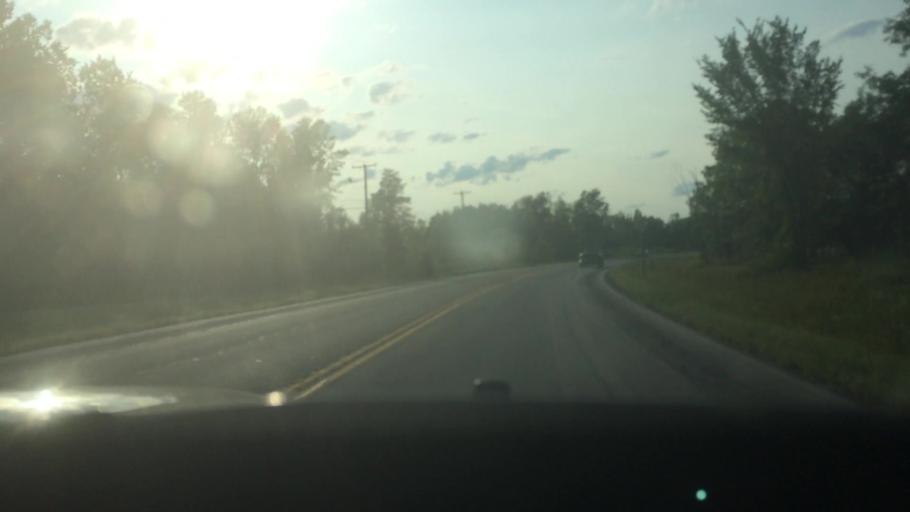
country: US
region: New York
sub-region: St. Lawrence County
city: Ogdensburg
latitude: 44.6725
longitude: -75.4298
